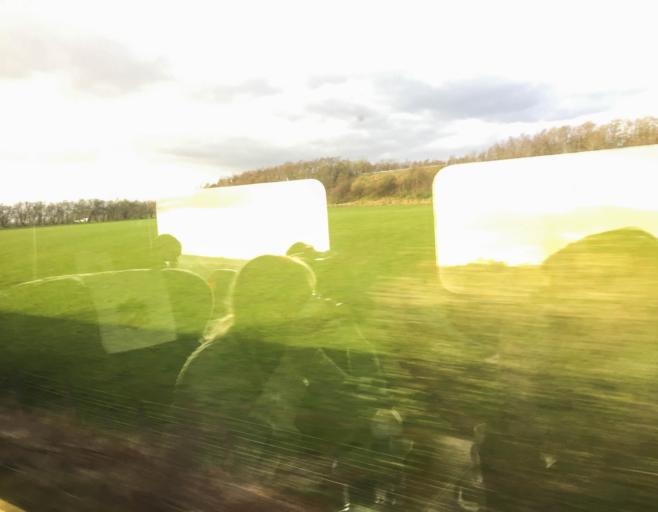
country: GB
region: Scotland
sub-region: Dumfries and Galloway
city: Annan
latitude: 55.0460
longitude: -3.2053
